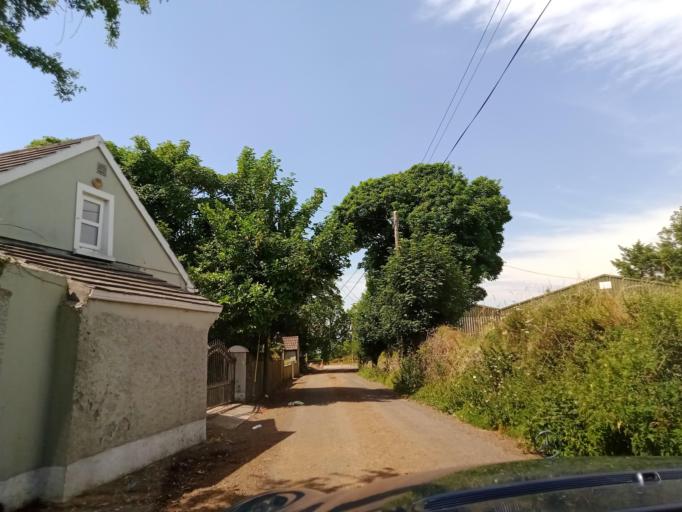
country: IE
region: Leinster
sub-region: Kilkenny
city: Mooncoin
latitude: 52.2663
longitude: -7.2313
